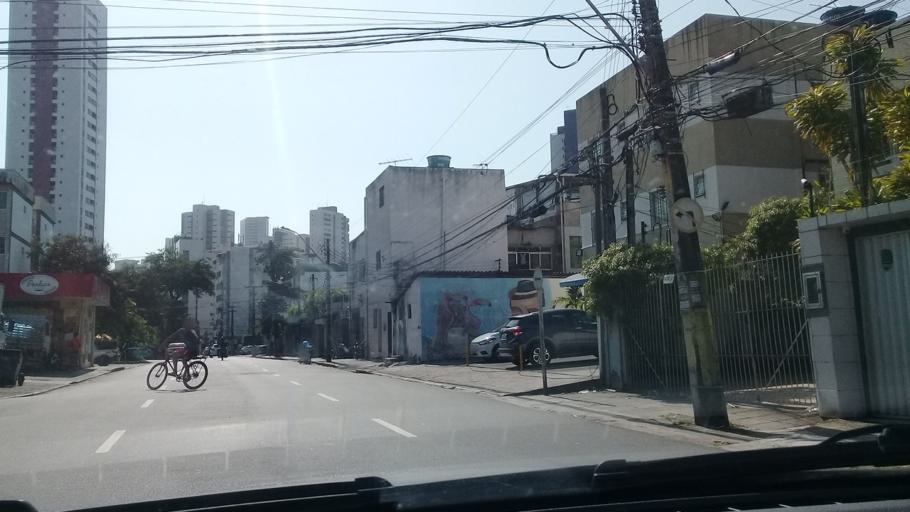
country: BR
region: Pernambuco
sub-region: Recife
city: Recife
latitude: -8.1355
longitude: -34.9077
